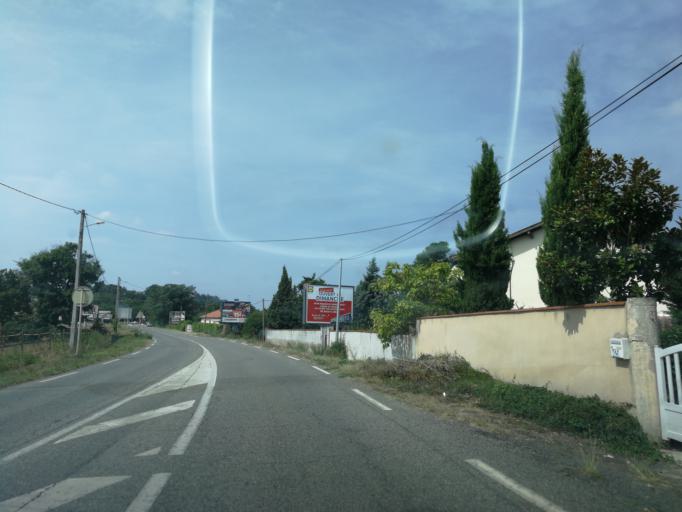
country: FR
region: Midi-Pyrenees
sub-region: Departement de la Haute-Garonne
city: Cornebarrieu
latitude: 43.6513
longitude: 1.3387
